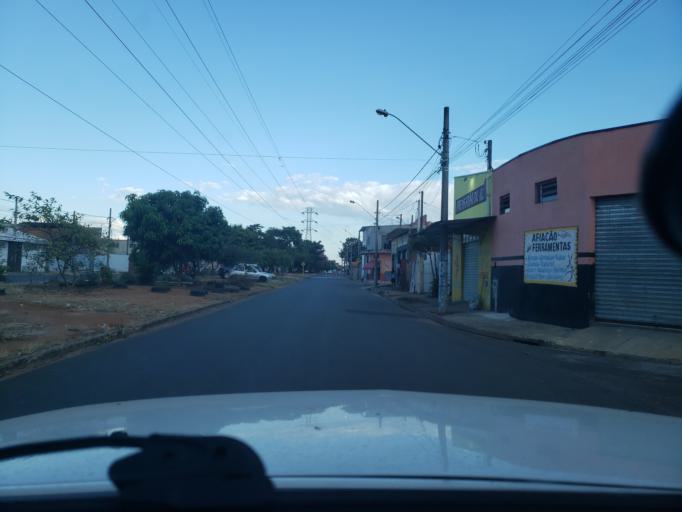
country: BR
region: Sao Paulo
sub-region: Moji-Guacu
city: Mogi-Gaucu
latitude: -22.3255
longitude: -46.9215
